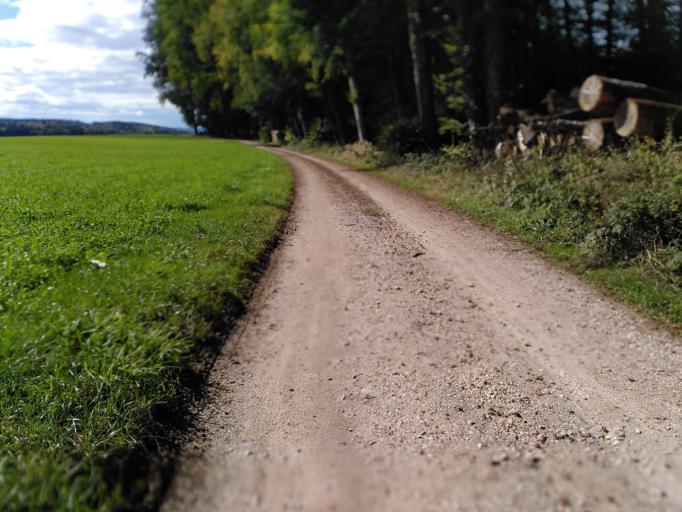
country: CH
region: Bern
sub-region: Oberaargau
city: Seeberg
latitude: 47.1306
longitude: 7.6478
